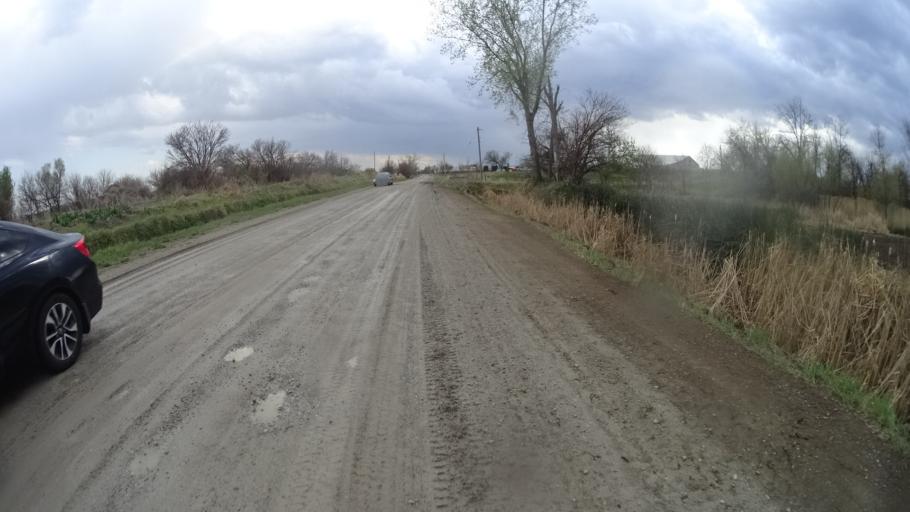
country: US
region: Nebraska
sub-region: Sarpy County
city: Offutt Air Force Base
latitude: 41.0789
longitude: -95.9200
